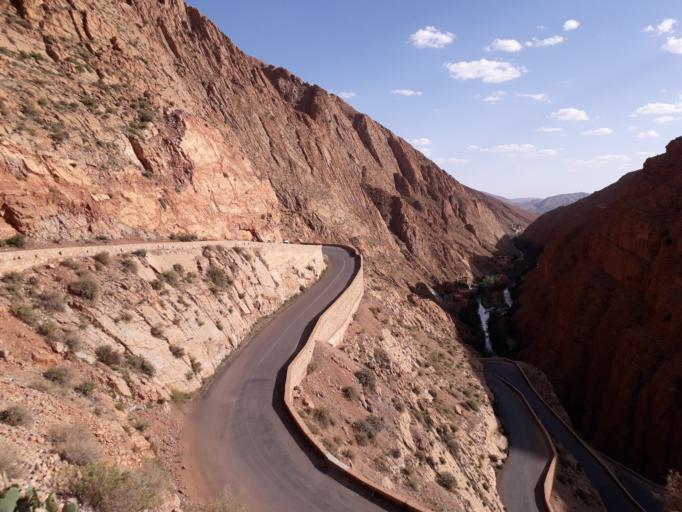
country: MA
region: Souss-Massa-Draa
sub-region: Ouarzazate
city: Imider
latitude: 31.5286
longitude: -5.9250
